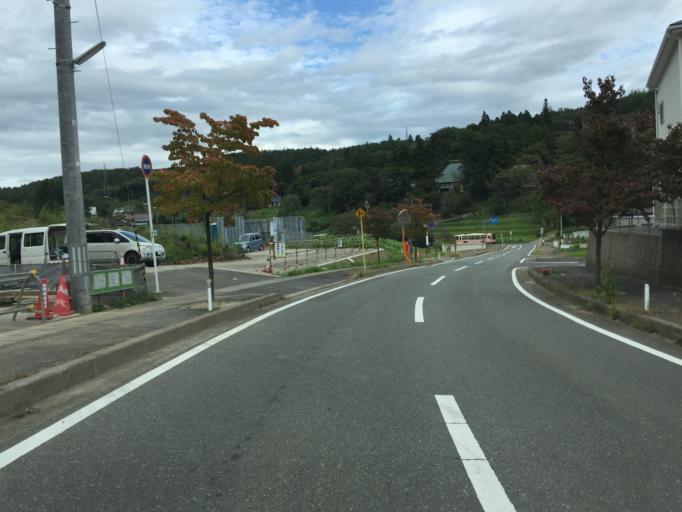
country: JP
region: Fukushima
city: Fukushima-shi
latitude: 37.6974
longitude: 140.4878
